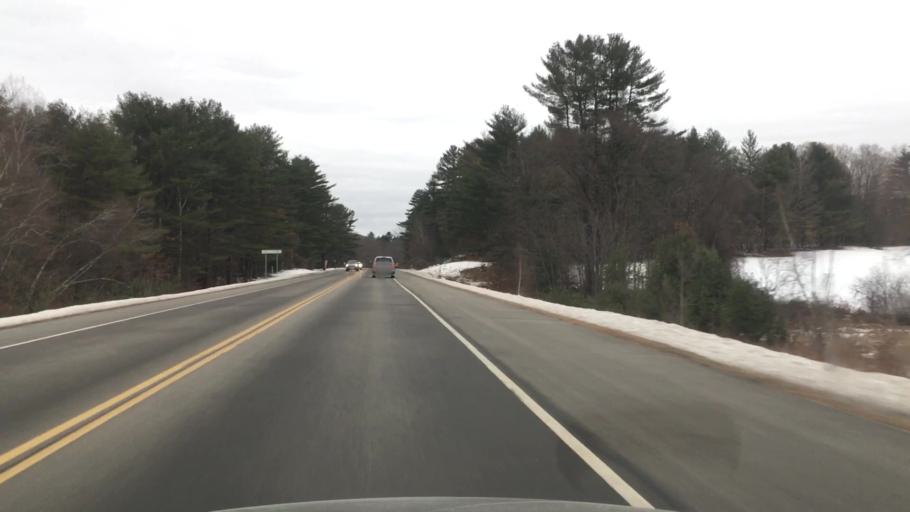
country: US
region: New Hampshire
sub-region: Merrimack County
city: Sutton
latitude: 43.2650
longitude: -71.9533
